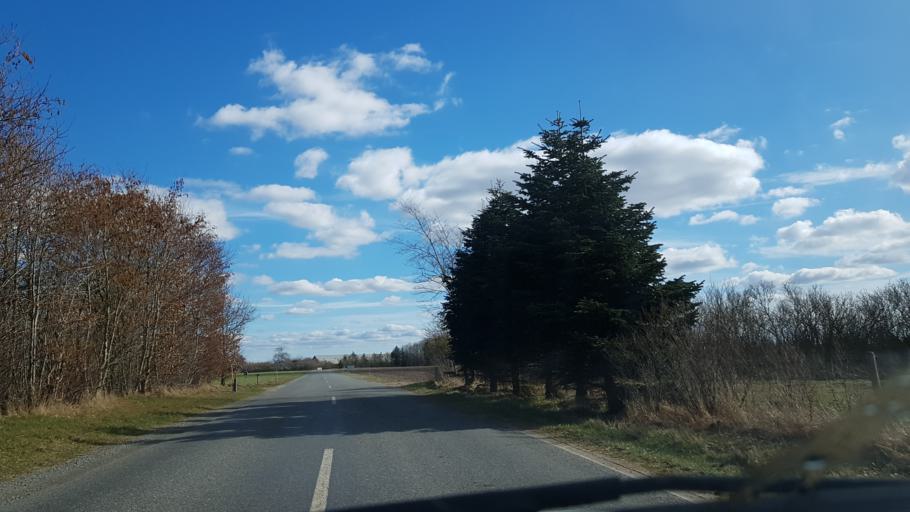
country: DK
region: South Denmark
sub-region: Esbjerg Kommune
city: Ribe
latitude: 55.4004
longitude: 8.8342
